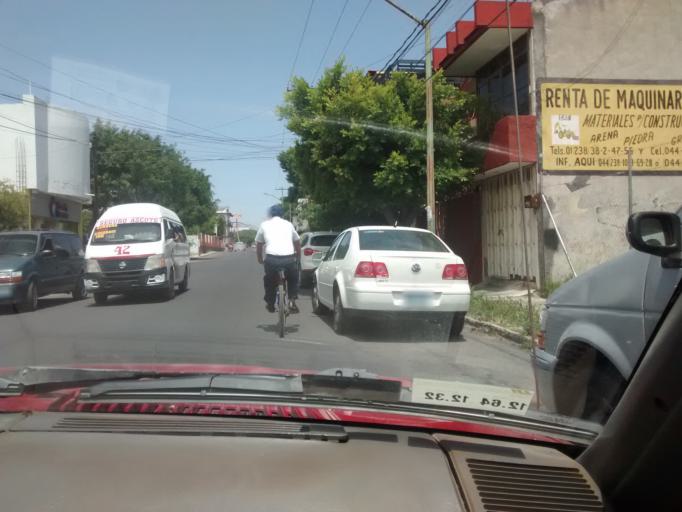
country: MX
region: Puebla
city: Tehuacan
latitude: 18.4604
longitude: -97.4114
